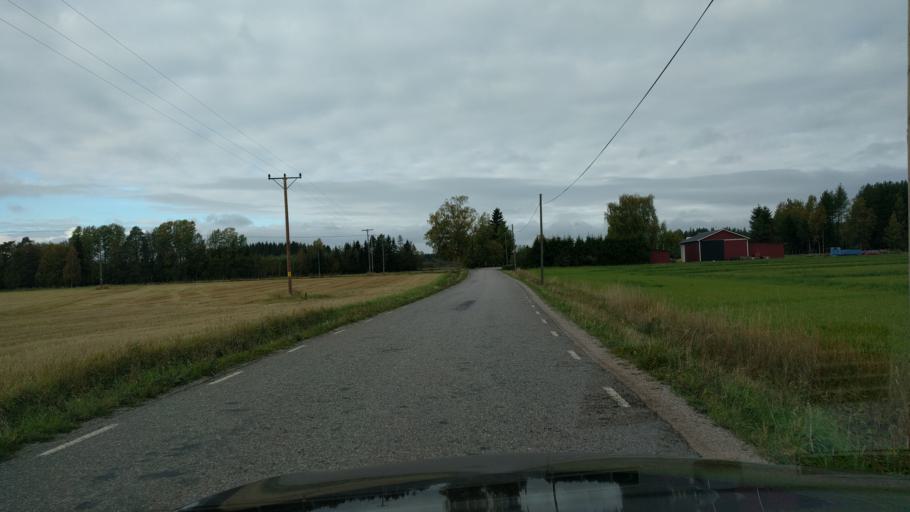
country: SE
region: Uppsala
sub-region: Osthammars Kommun
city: Bjorklinge
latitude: 60.1570
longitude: 17.5460
